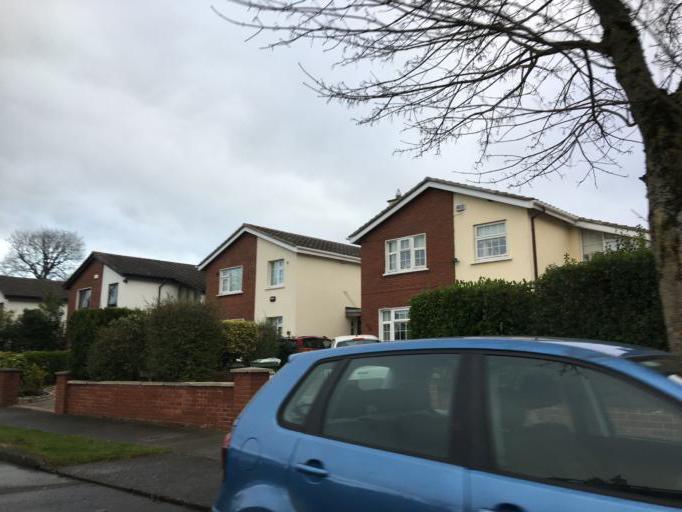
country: IE
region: Leinster
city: Castleknock
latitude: 53.3717
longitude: -6.3651
